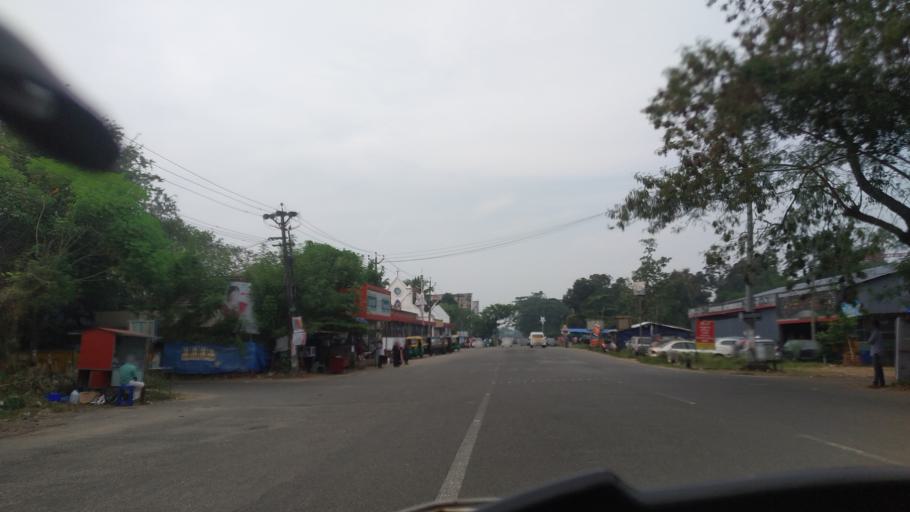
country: IN
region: Kerala
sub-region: Ernakulam
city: Elur
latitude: 10.0579
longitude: 76.2908
